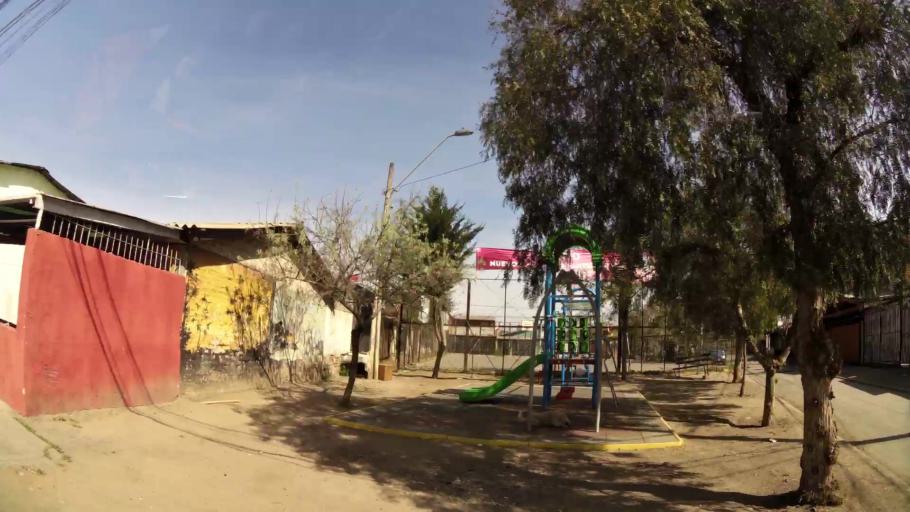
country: CL
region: Santiago Metropolitan
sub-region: Provincia de Santiago
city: La Pintana
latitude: -33.5340
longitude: -70.6042
